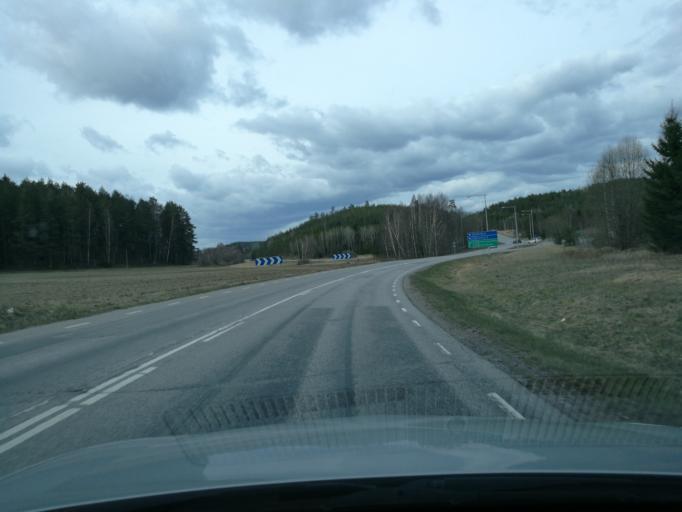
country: SE
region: Soedermanland
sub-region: Gnesta Kommun
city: Gnesta
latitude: 58.9081
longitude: 17.3263
